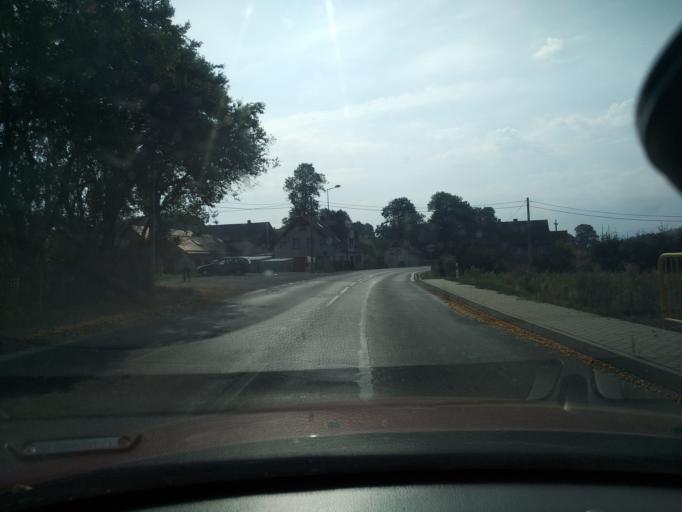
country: PL
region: Lower Silesian Voivodeship
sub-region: Powiat jeleniogorski
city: Stara Kamienica
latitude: 50.9544
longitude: 15.5785
